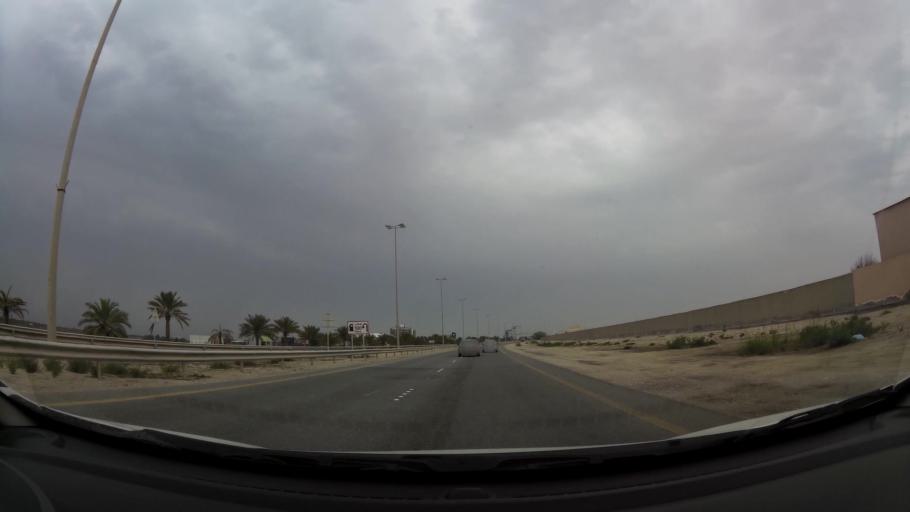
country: BH
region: Central Governorate
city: Dar Kulayb
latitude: 26.0215
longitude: 50.4904
